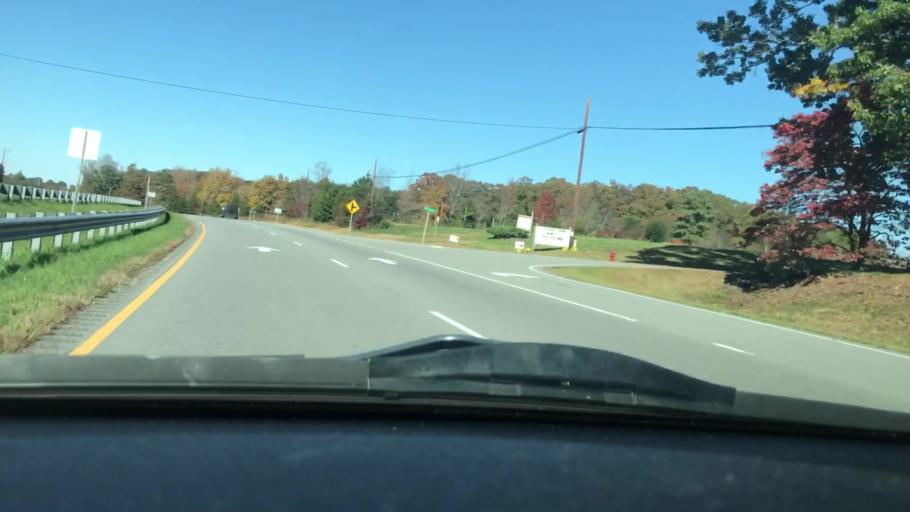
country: US
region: North Carolina
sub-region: Rockingham County
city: Madison
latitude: 36.3384
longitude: -79.9437
